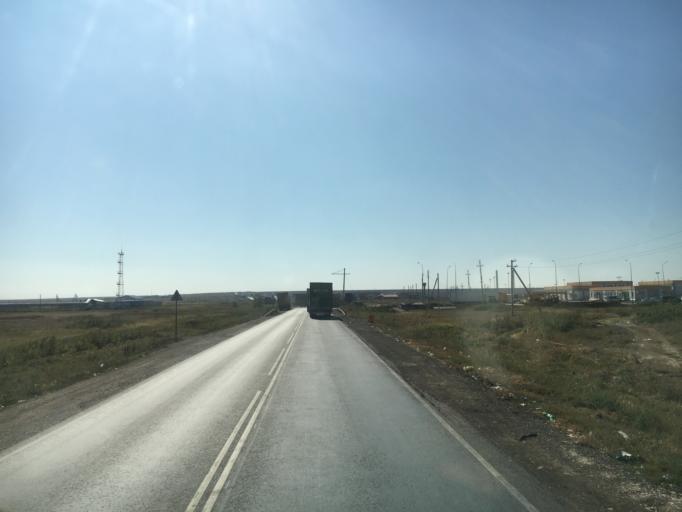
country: KZ
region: Batys Qazaqstan
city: Peremetnoe
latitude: 51.6810
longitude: 51.0025
